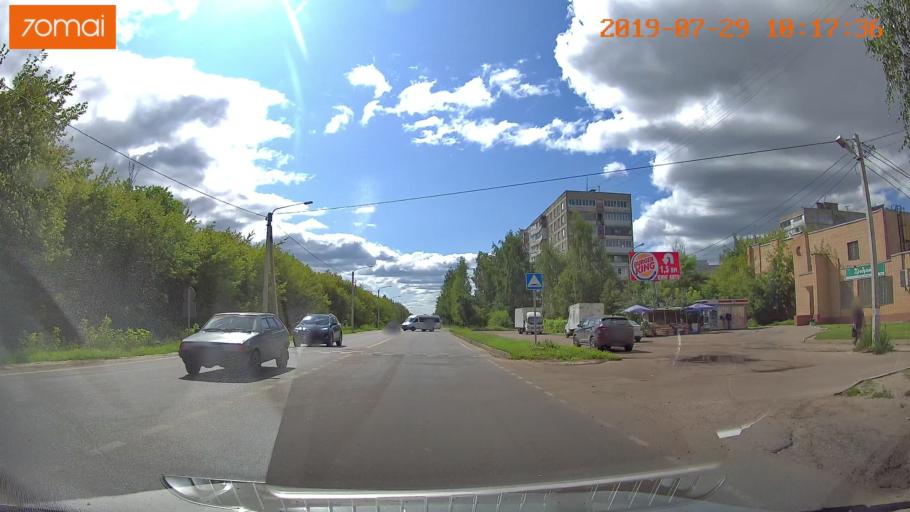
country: RU
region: Moskovskaya
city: Voskresensk
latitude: 55.3103
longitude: 38.6557
